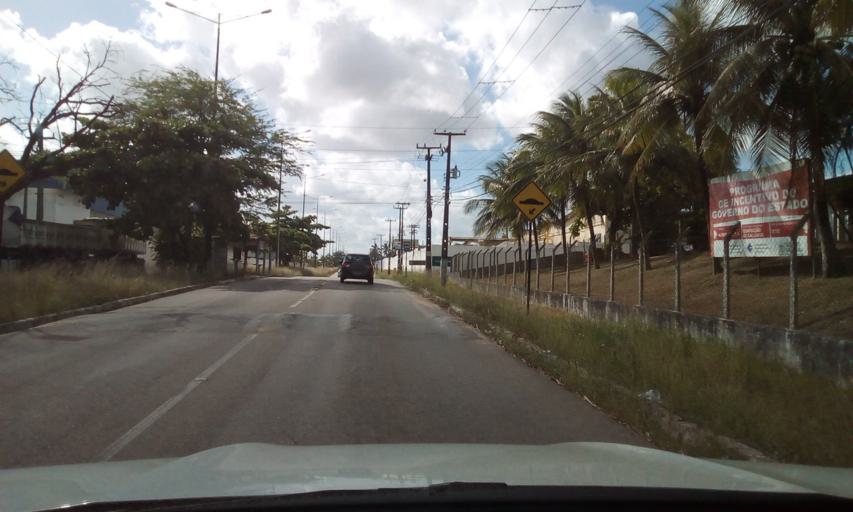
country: BR
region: Paraiba
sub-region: Bayeux
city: Bayeux
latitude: -7.1788
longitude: -34.9054
